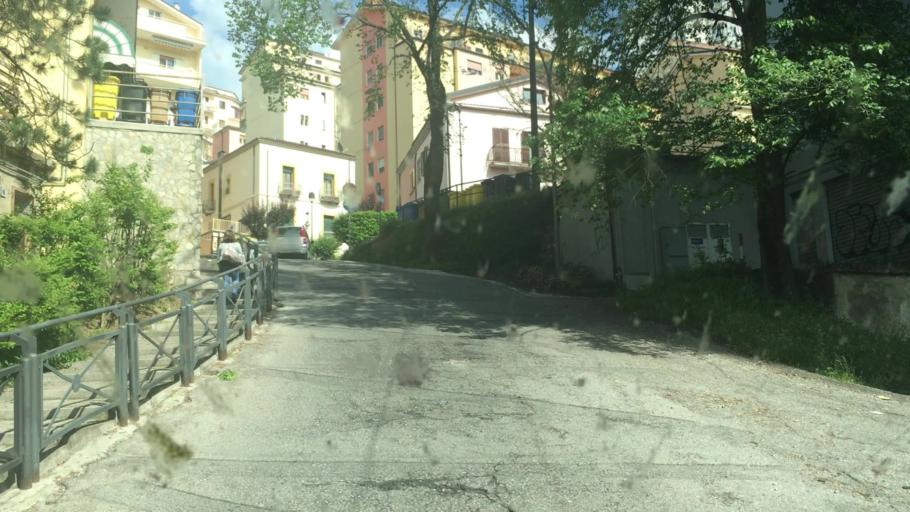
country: IT
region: Basilicate
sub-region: Provincia di Potenza
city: Potenza
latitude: 40.6418
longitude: 15.8041
